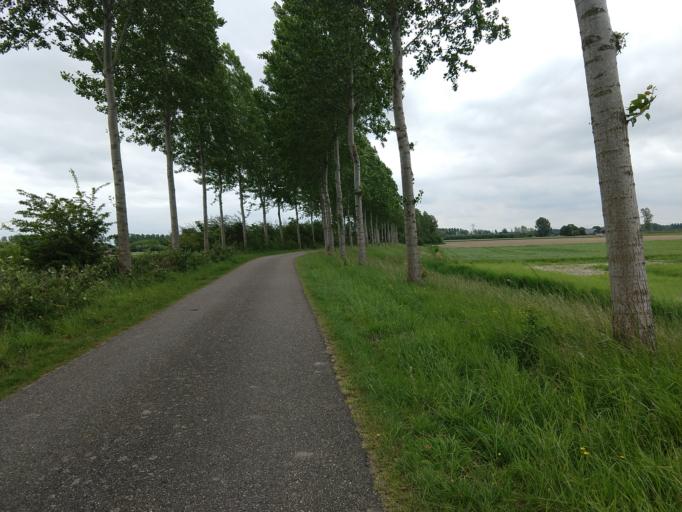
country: NL
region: Zeeland
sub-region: Gemeente Borsele
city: Borssele
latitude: 51.4577
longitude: 3.7958
